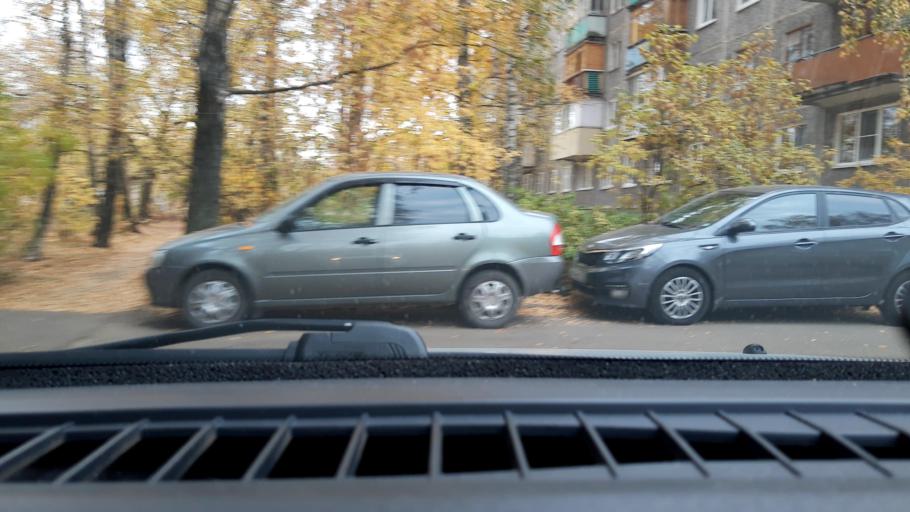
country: RU
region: Nizjnij Novgorod
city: Gorbatovka
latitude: 56.3536
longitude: 43.8391
